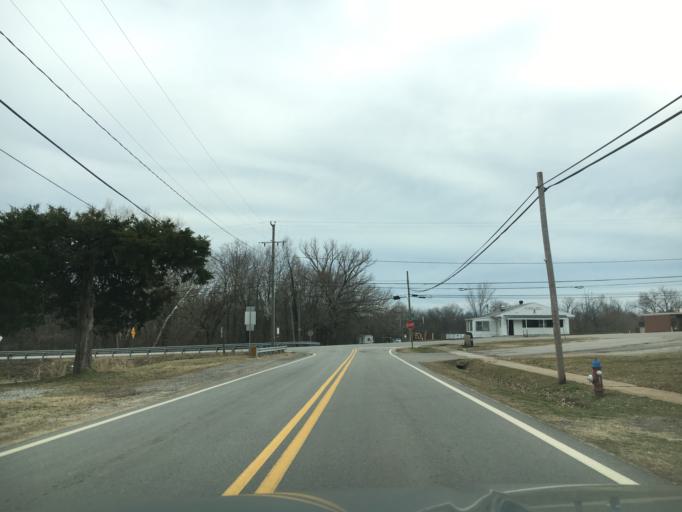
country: US
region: Virginia
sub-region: Charlotte County
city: Charlotte Court House
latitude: 37.0812
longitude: -78.7463
